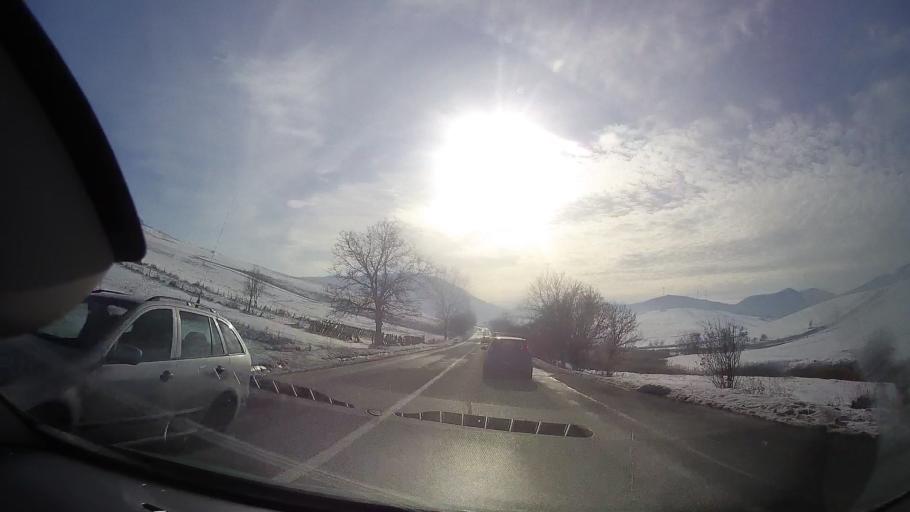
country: RO
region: Neamt
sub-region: Comuna Garcina
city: Garcina
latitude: 46.9867
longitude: 26.3600
